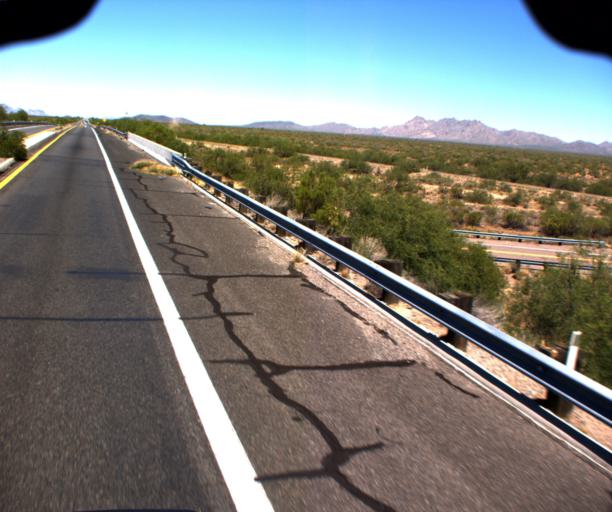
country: US
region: Arizona
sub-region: Yavapai County
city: Congress
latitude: 34.1231
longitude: -112.9501
